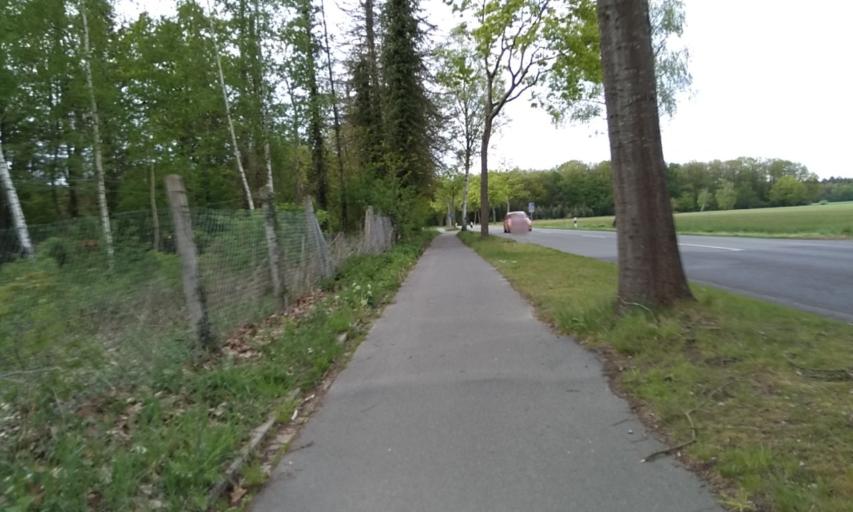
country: DE
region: Lower Saxony
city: Wohnste
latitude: 53.3917
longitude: 9.5393
